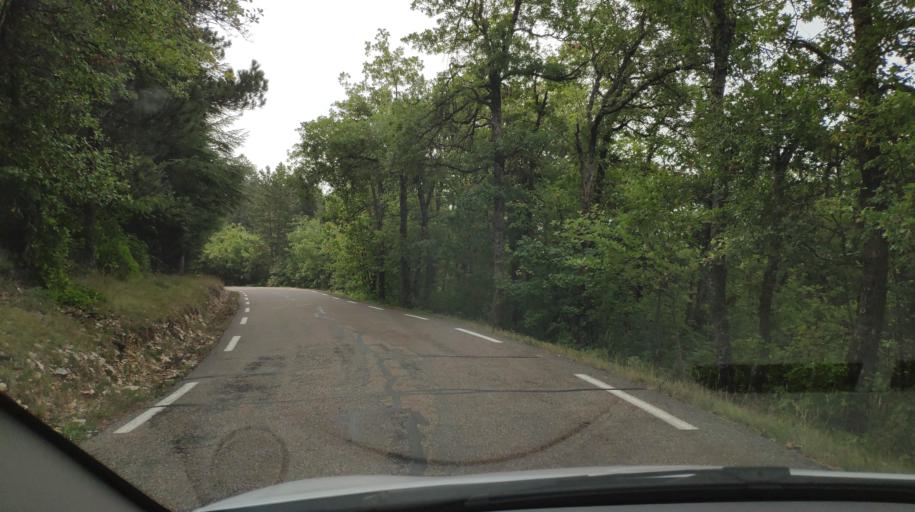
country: FR
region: Provence-Alpes-Cote d'Azur
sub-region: Departement du Vaucluse
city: Sault
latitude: 44.1519
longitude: 5.3547
